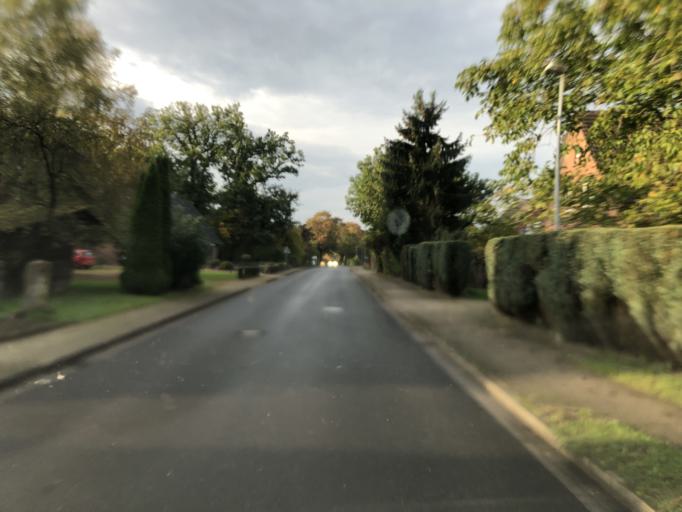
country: DE
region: Lower Saxony
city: Neu Wulmstorf
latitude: 53.4438
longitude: 9.8041
